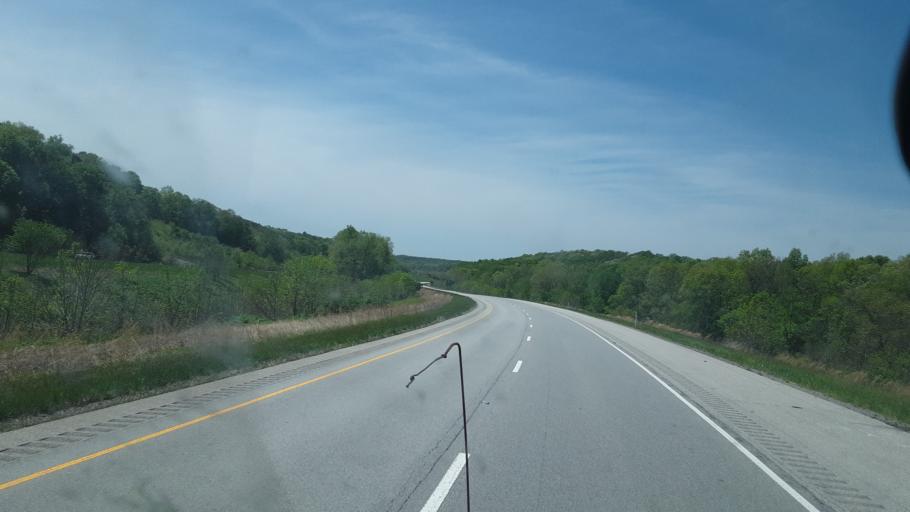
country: US
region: Indiana
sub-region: Dubois County
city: Ferdinand
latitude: 38.2340
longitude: -86.6720
